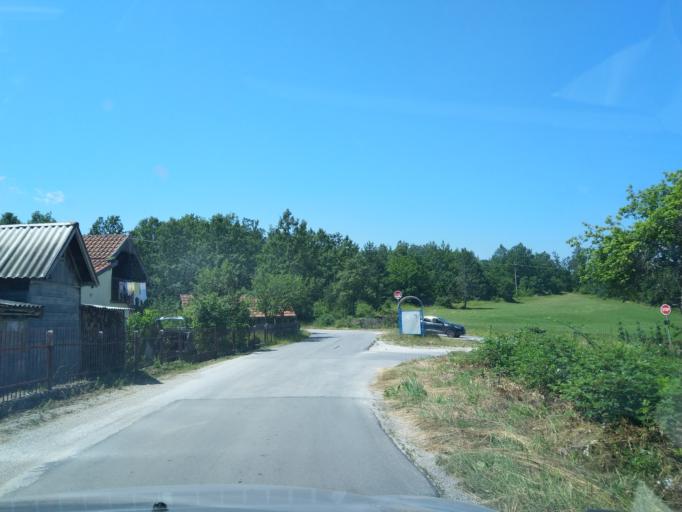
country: RS
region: Central Serbia
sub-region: Zlatiborski Okrug
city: Uzice
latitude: 43.7849
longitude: 19.8559
